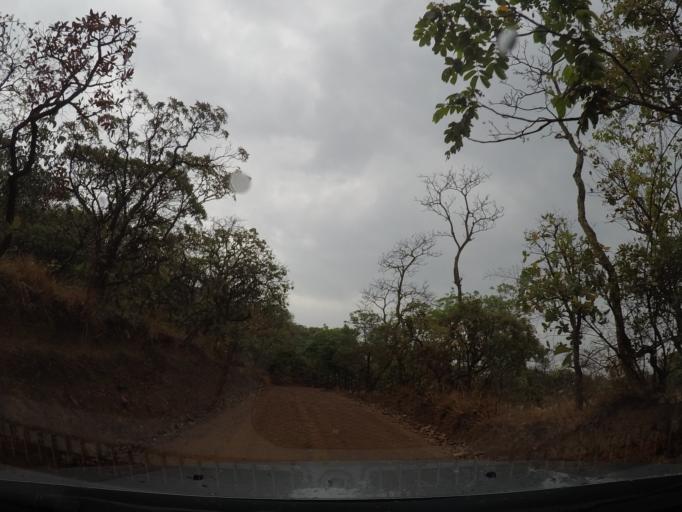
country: BR
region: Goias
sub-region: Pirenopolis
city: Pirenopolis
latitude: -15.8202
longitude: -48.8944
